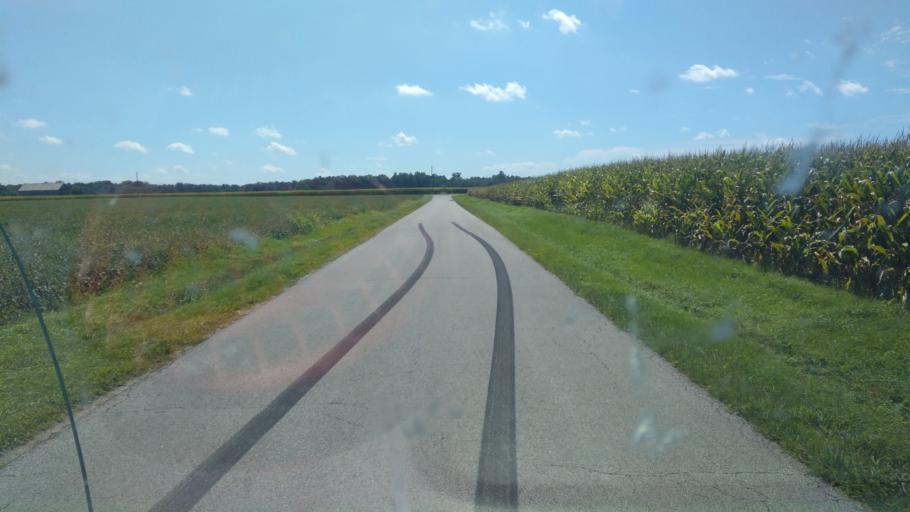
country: US
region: Ohio
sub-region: Crawford County
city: Bucyrus
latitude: 40.7924
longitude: -83.0505
